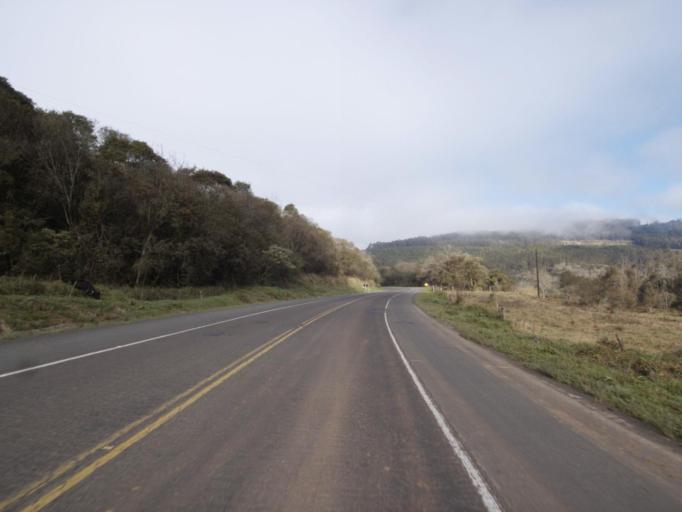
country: BR
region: Rio Grande do Sul
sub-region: Frederico Westphalen
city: Frederico Westphalen
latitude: -27.0163
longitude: -53.2280
